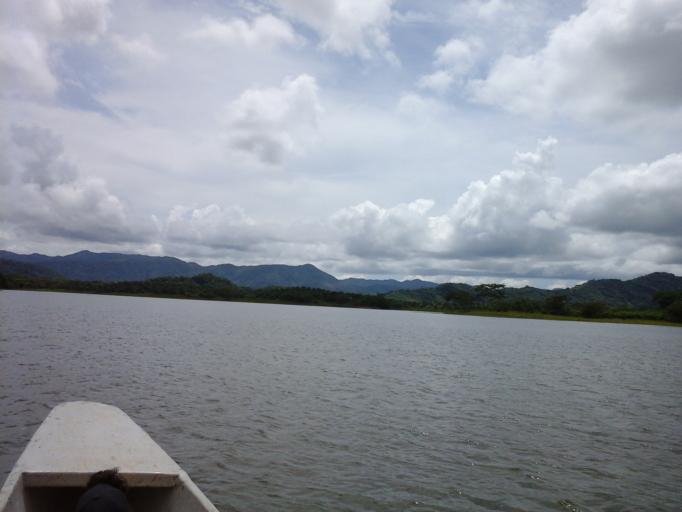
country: CO
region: Bolivar
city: San Cristobal
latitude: 9.8724
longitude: -75.2960
